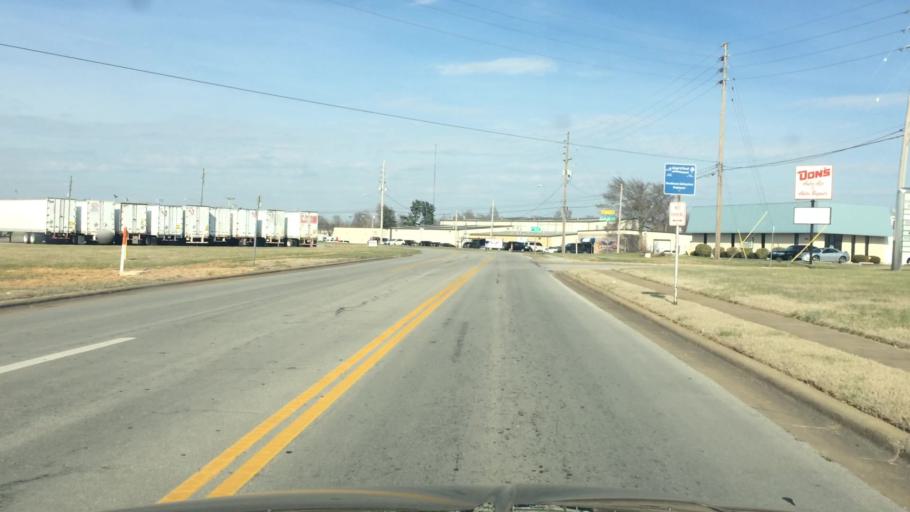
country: US
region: Missouri
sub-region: Greene County
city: Springfield
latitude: 37.2143
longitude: -93.2562
